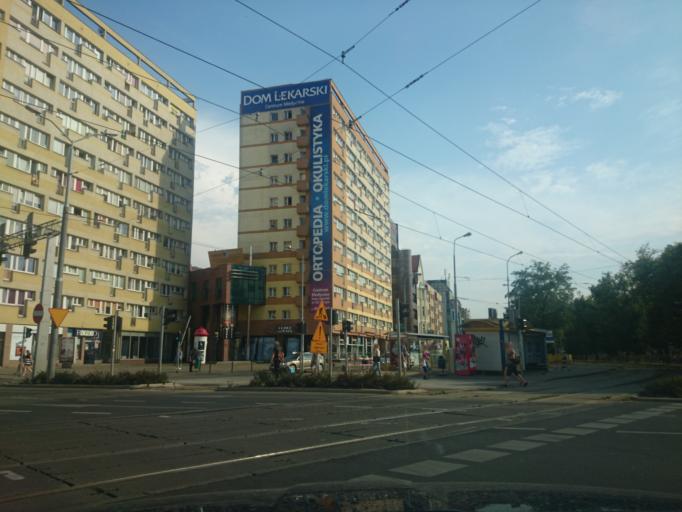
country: PL
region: West Pomeranian Voivodeship
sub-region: Szczecin
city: Szczecin
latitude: 53.4286
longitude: 14.5526
